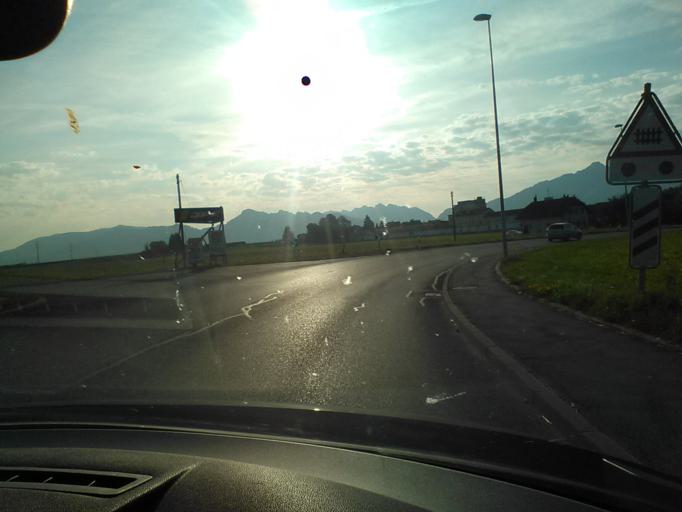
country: CH
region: Fribourg
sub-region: Gruyere District
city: Vuadens
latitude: 46.6189
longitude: 7.0164
